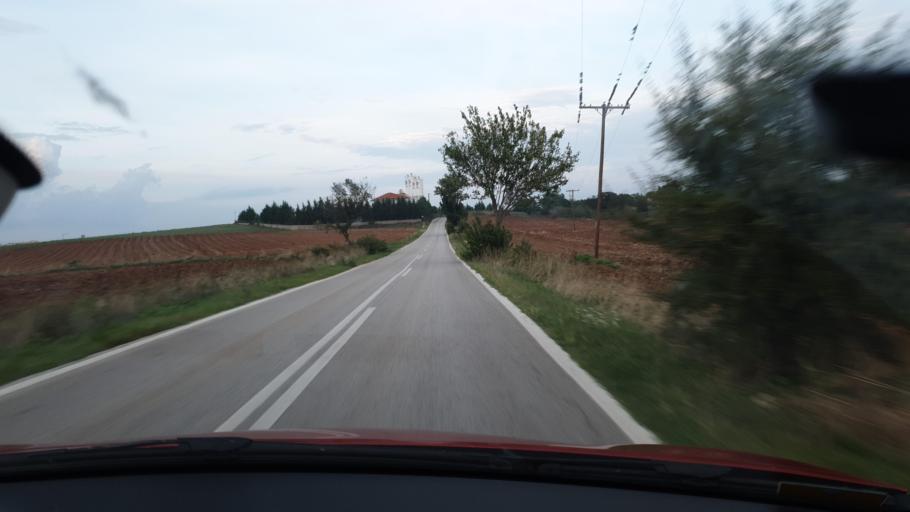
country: GR
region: Central Macedonia
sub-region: Nomos Kilkis
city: Kristoni
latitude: 40.9548
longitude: 22.8386
